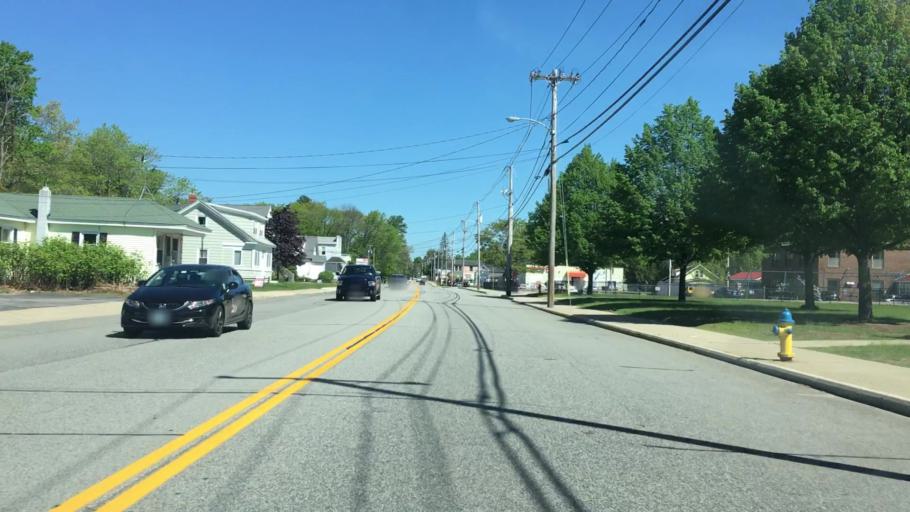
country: US
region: Maine
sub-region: York County
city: Springvale
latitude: 43.4525
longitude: -70.7885
